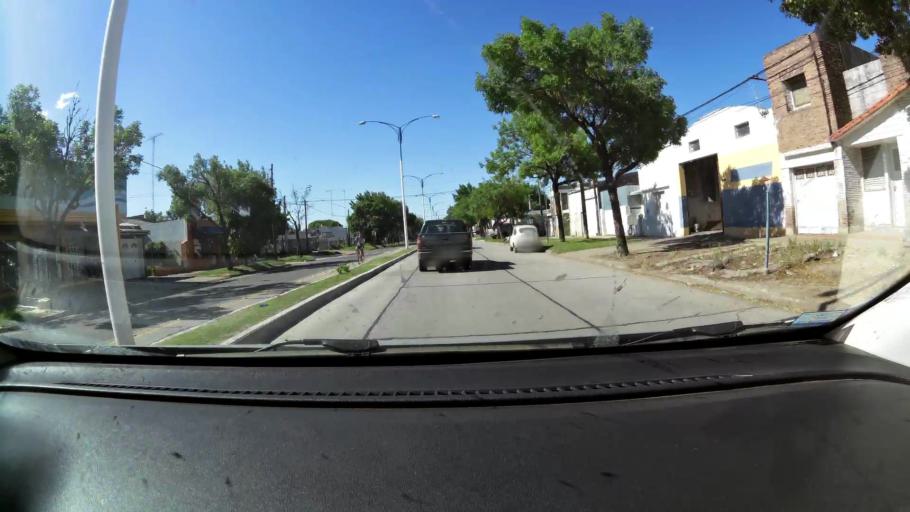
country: AR
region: Santa Fe
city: Rafaela
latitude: -31.2414
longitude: -61.4890
